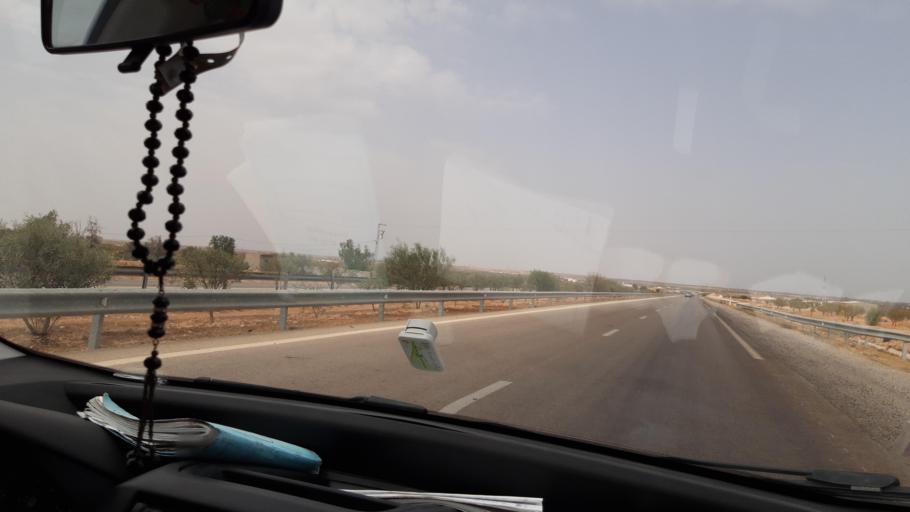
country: TN
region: Safaqis
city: Sfax
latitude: 34.8642
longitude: 10.6889
